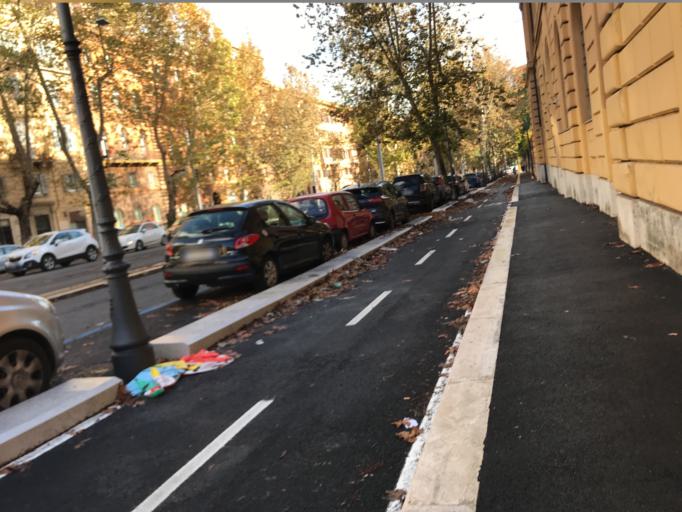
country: IT
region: Latium
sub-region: Citta metropolitana di Roma Capitale
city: Rome
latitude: 41.9119
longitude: 12.5055
